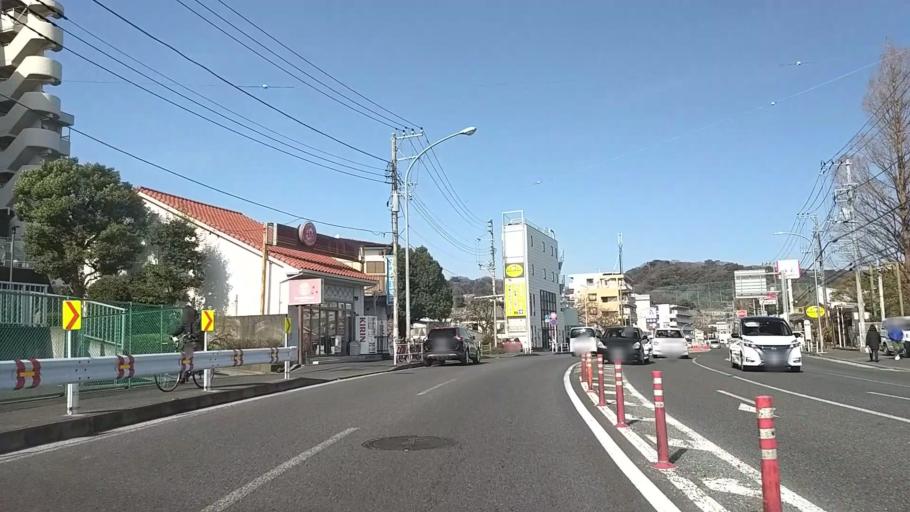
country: JP
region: Kanagawa
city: Zushi
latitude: 35.3448
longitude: 139.6109
